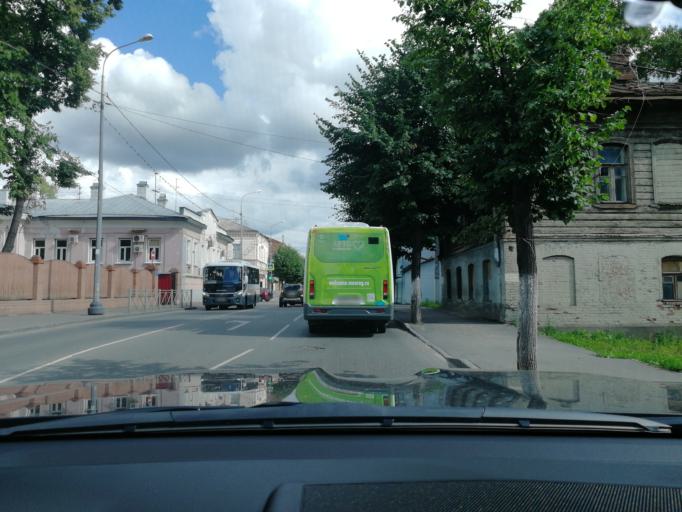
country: RU
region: Moskovskaya
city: Serpukhov
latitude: 54.9162
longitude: 37.4133
